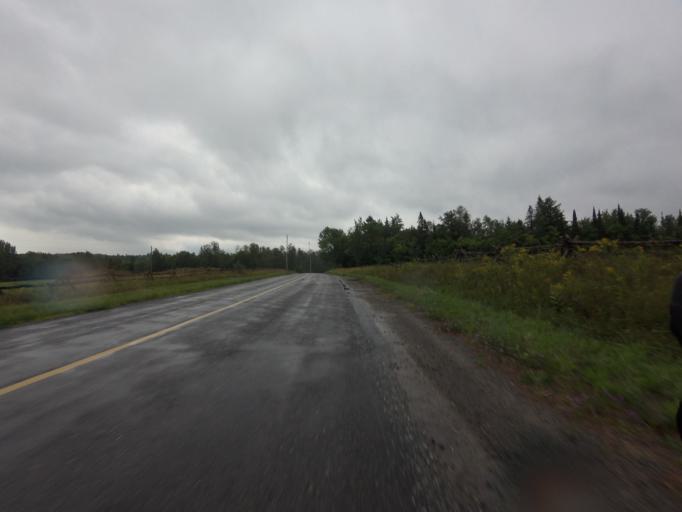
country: CA
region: Ontario
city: Renfrew
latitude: 45.0657
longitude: -76.6344
